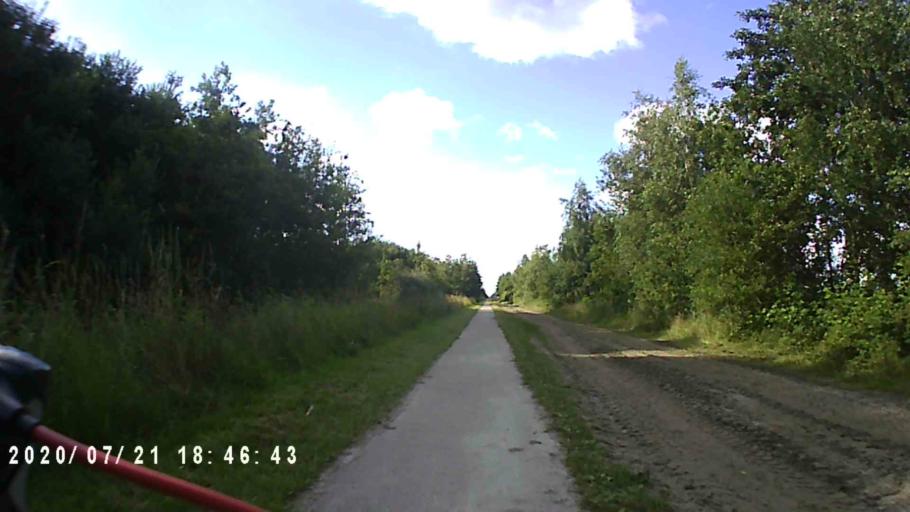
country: NL
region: Groningen
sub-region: Gemeente Hoogezand-Sappemeer
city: Hoogezand
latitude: 53.2103
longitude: 6.7484
